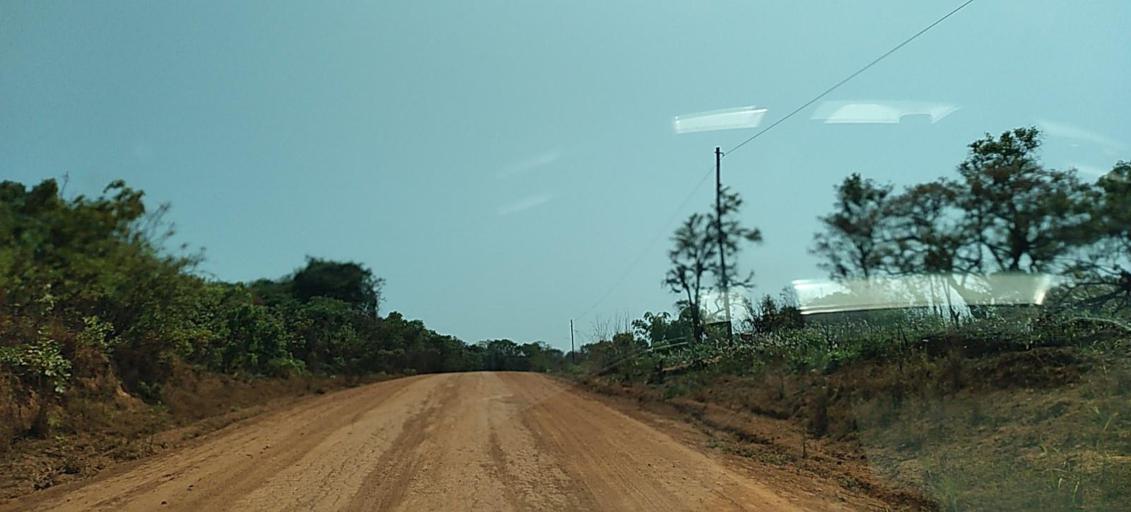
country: ZM
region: North-Western
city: Kansanshi
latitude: -11.9941
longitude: 26.6166
